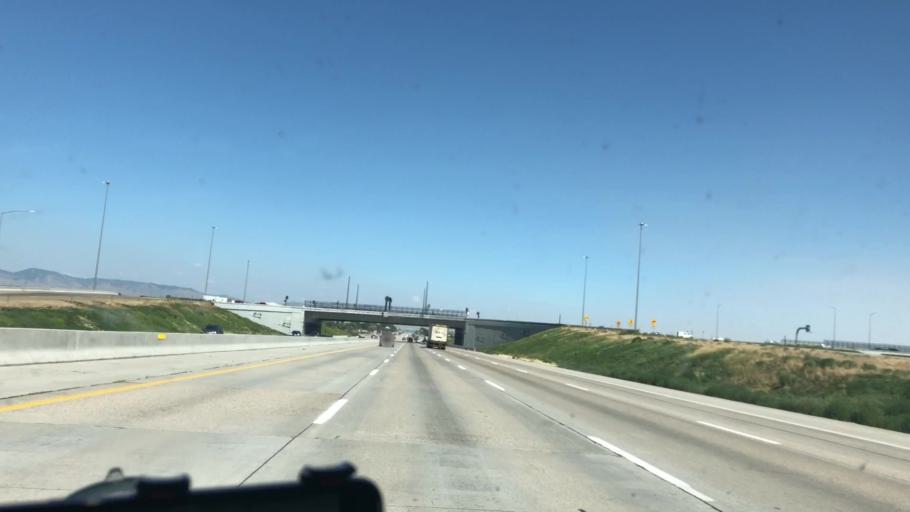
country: US
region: Idaho
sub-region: Ada County
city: Meridian
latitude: 43.5934
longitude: -116.4380
